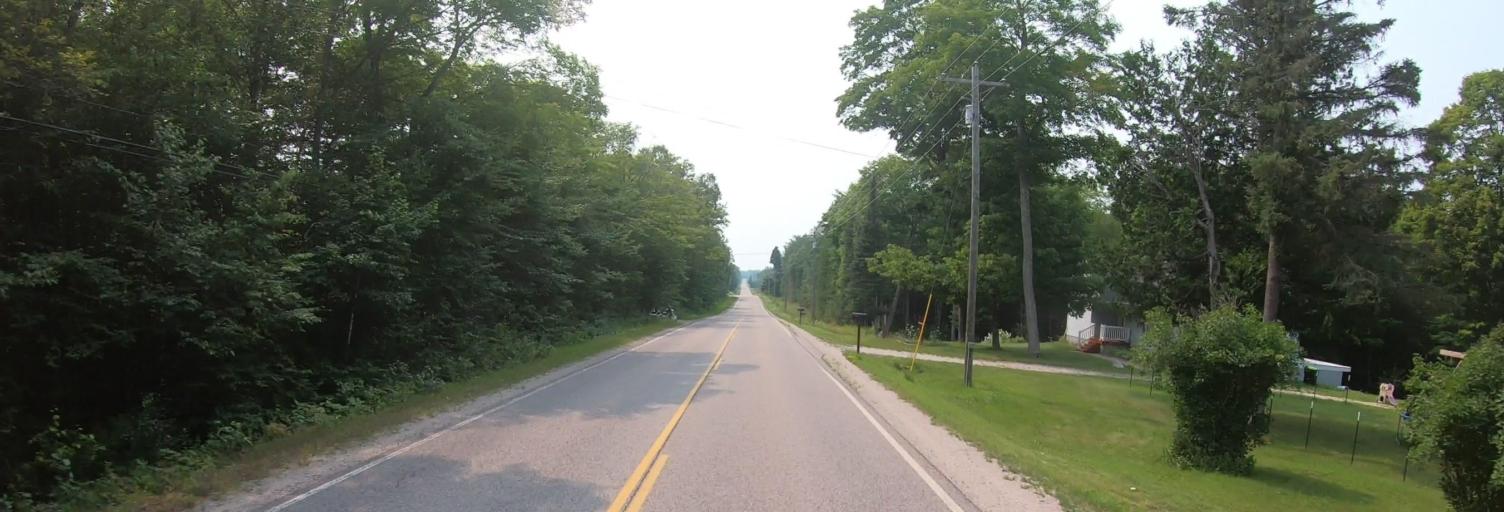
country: CA
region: Ontario
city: Thessalon
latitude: 46.0002
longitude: -83.9551
